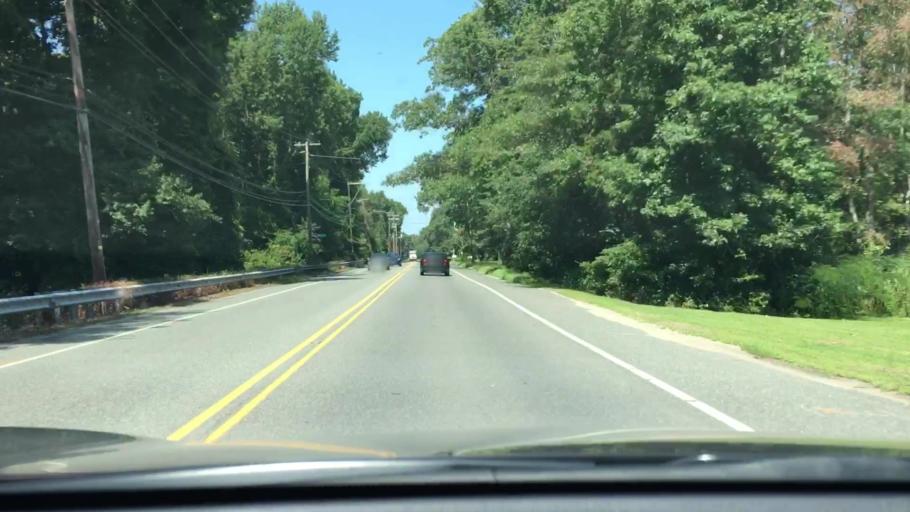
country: US
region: New Jersey
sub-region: Cumberland County
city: Laurel Lake
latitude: 39.3372
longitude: -75.0258
